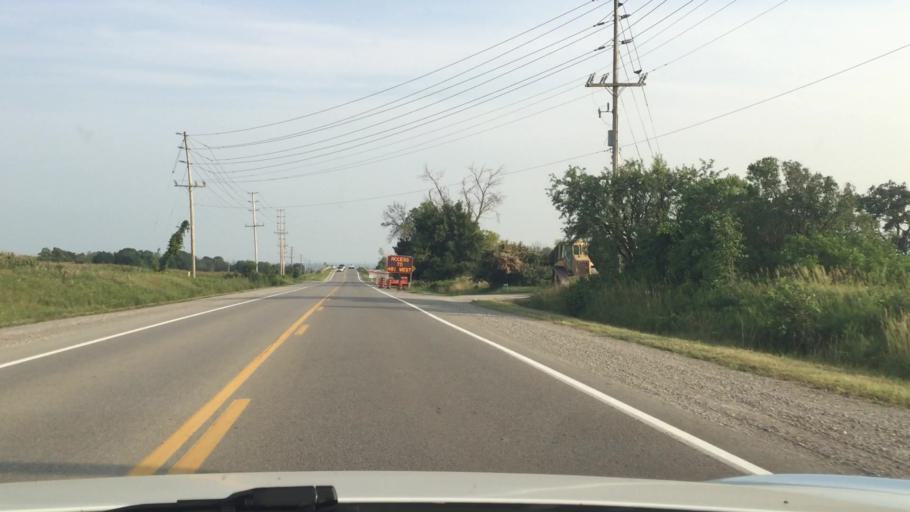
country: CA
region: Ontario
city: Oshawa
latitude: 43.8872
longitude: -78.7673
